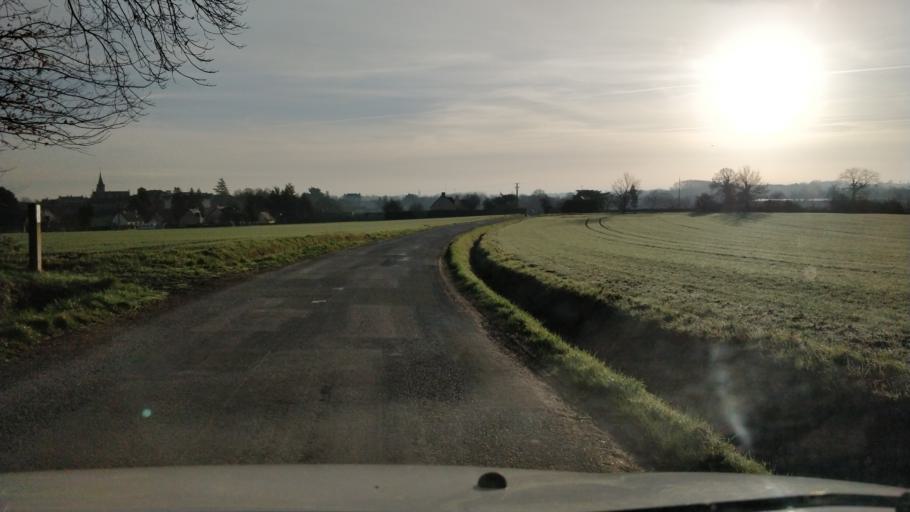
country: FR
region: Brittany
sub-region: Departement d'Ille-et-Vilaine
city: Bais
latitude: 48.0097
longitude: -1.2992
